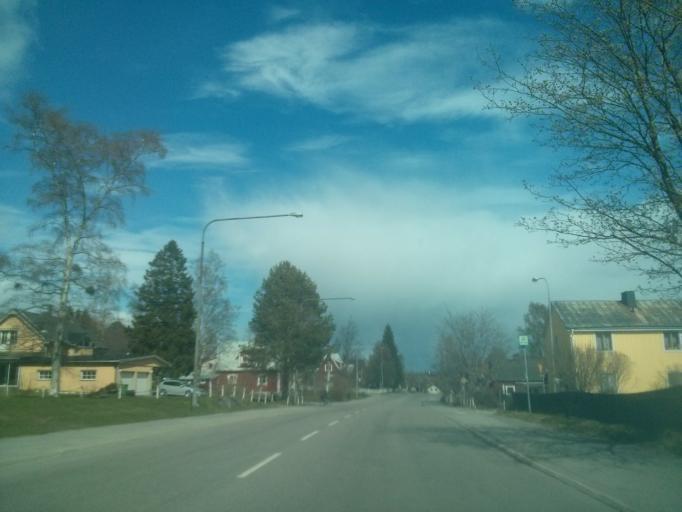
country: SE
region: Vaesternorrland
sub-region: Haernoesands Kommun
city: Haernoesand
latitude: 62.6338
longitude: 17.9148
